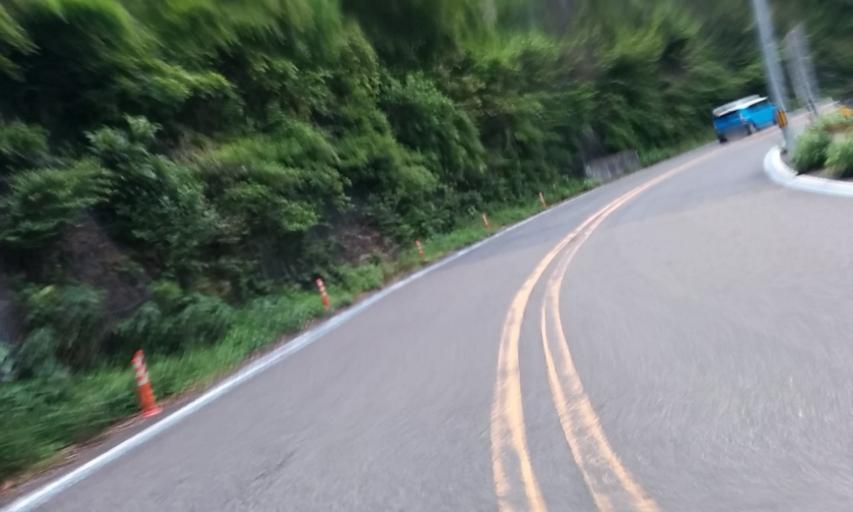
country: JP
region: Ehime
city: Niihama
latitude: 33.9200
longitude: 133.3124
